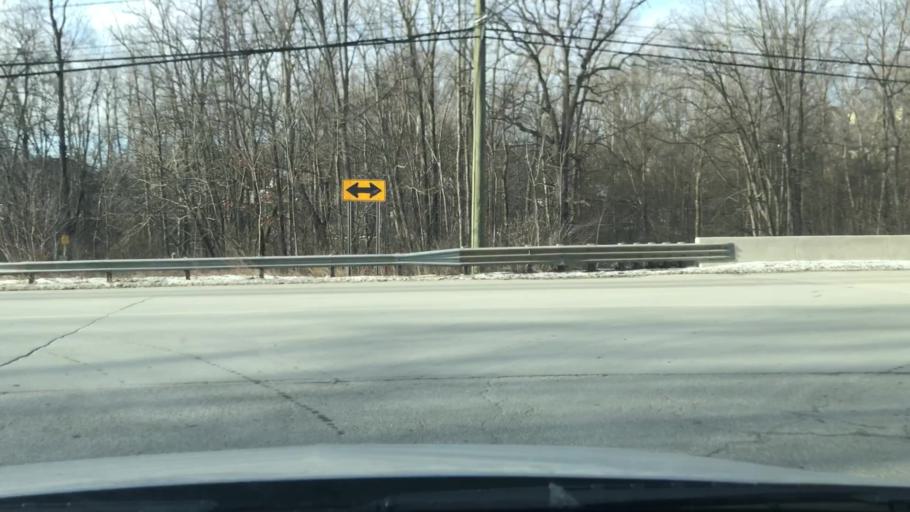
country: US
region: Michigan
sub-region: Oakland County
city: Rochester
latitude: 42.7309
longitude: -83.1591
